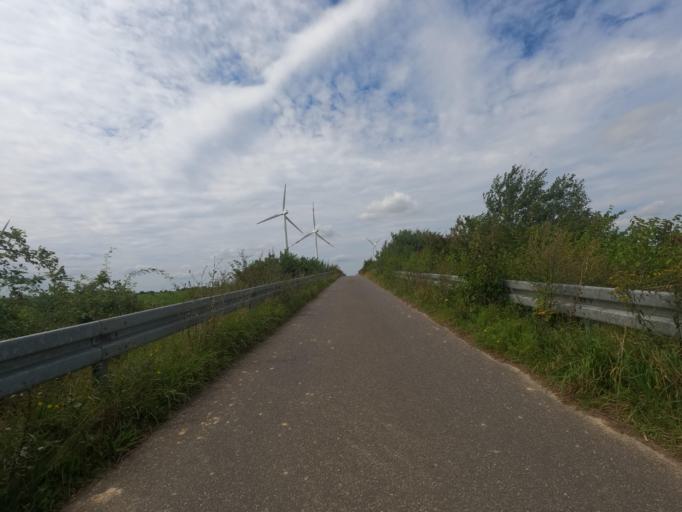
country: DE
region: North Rhine-Westphalia
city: Baesweiler
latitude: 50.9297
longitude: 6.1575
